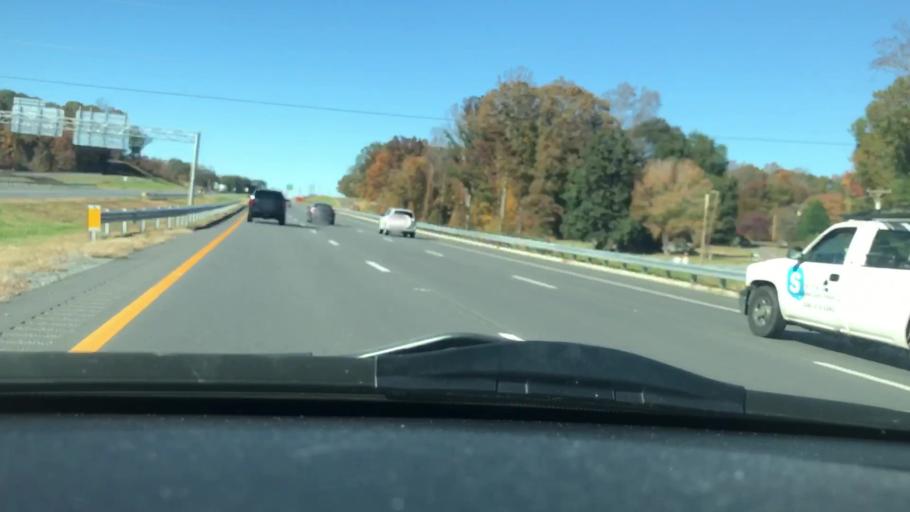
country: US
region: North Carolina
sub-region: Guilford County
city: Summerfield
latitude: 36.2304
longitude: -79.9150
